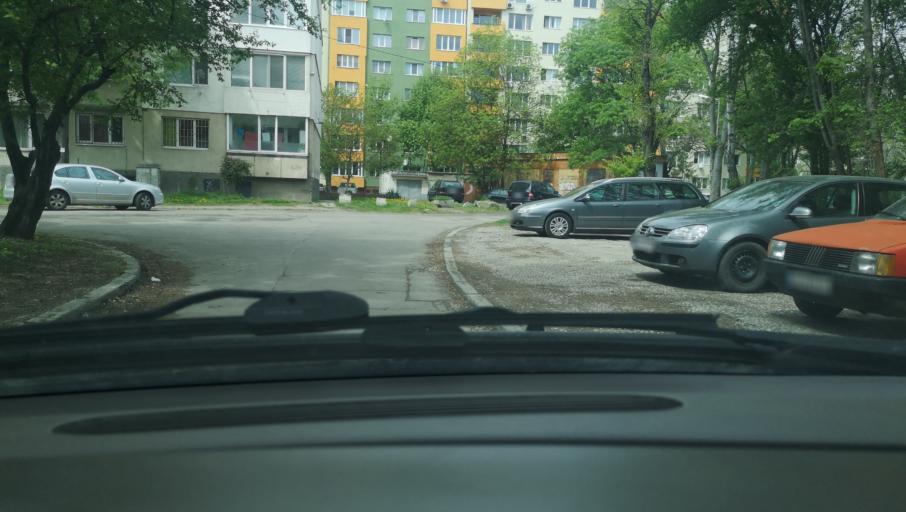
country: BG
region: Sofia-Capital
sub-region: Stolichna Obshtina
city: Sofia
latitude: 42.7101
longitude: 23.3534
